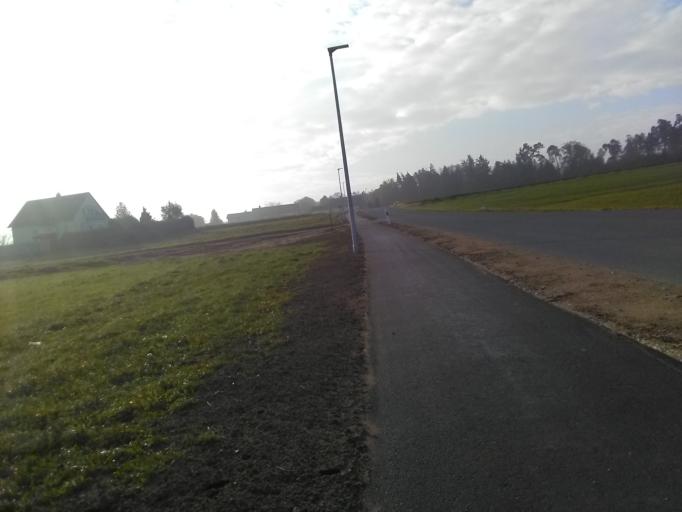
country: DE
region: Bavaria
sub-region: Regierungsbezirk Mittelfranken
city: Bruckberg
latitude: 49.3156
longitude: 10.7014
